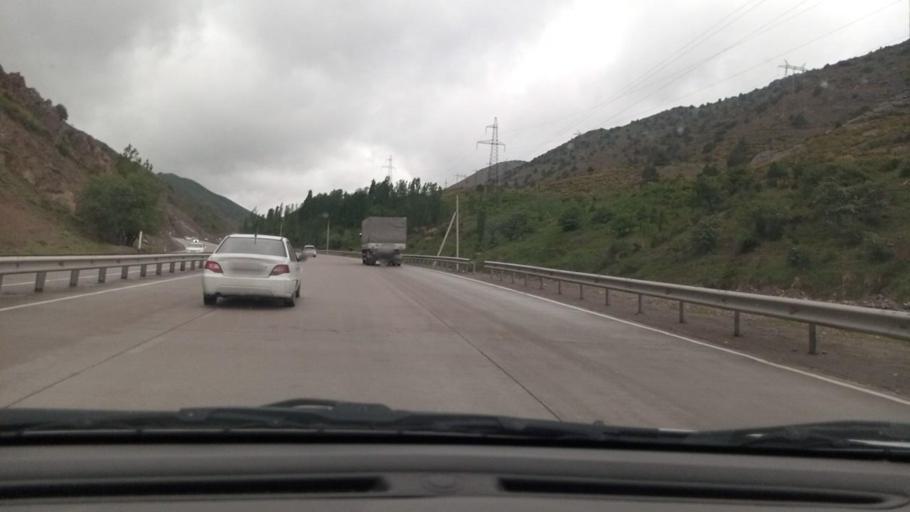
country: UZ
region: Toshkent
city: Angren
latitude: 41.0439
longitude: 70.5745
